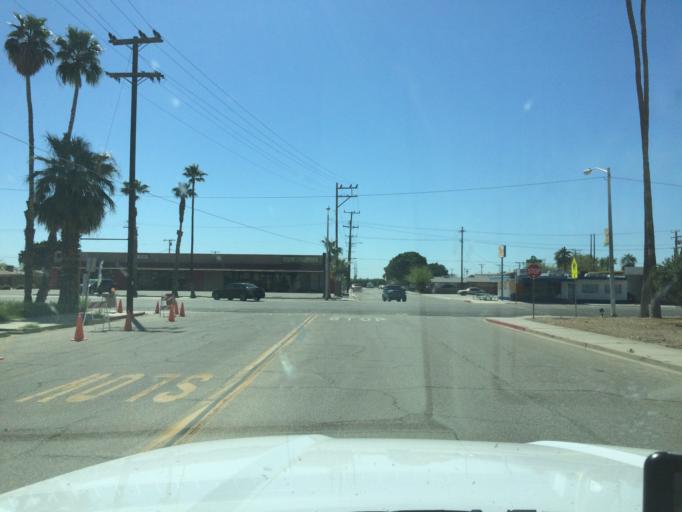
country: US
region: California
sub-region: Riverside County
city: Blythe
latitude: 33.6109
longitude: -114.5904
